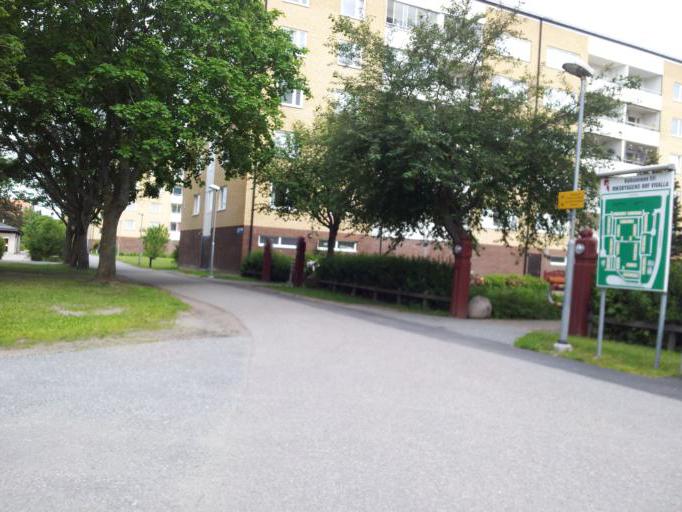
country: SE
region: Uppsala
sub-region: Uppsala Kommun
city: Gamla Uppsala
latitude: 59.8866
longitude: 17.6554
